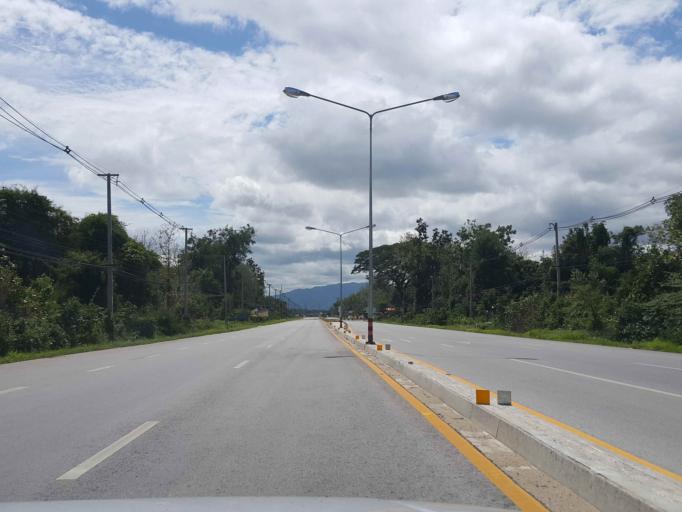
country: TH
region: Tak
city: Tak
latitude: 16.8866
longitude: 99.1830
